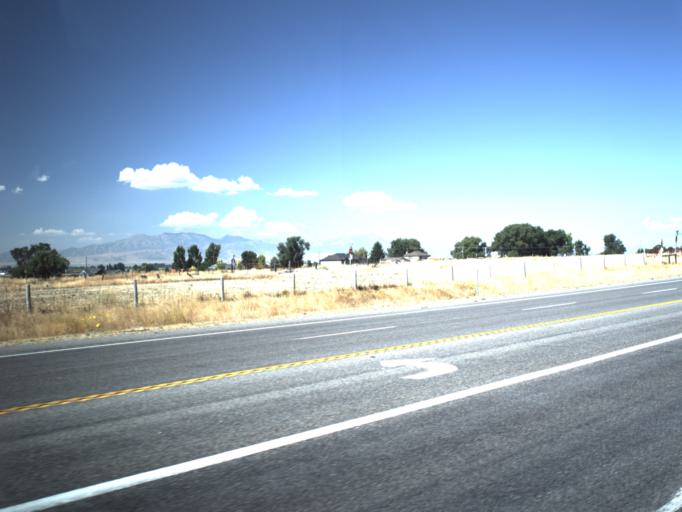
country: US
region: Utah
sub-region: Cache County
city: Richmond
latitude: 41.9480
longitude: -111.8134
